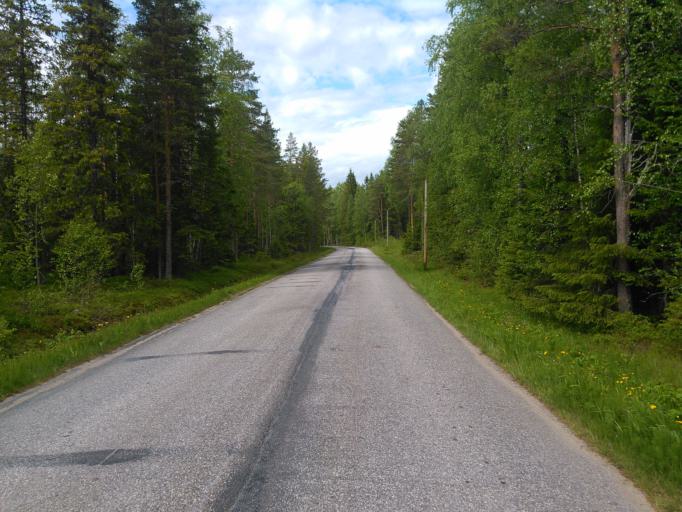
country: SE
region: Vaesterbotten
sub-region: Umea Kommun
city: Ersmark
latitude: 63.8750
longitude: 20.3262
